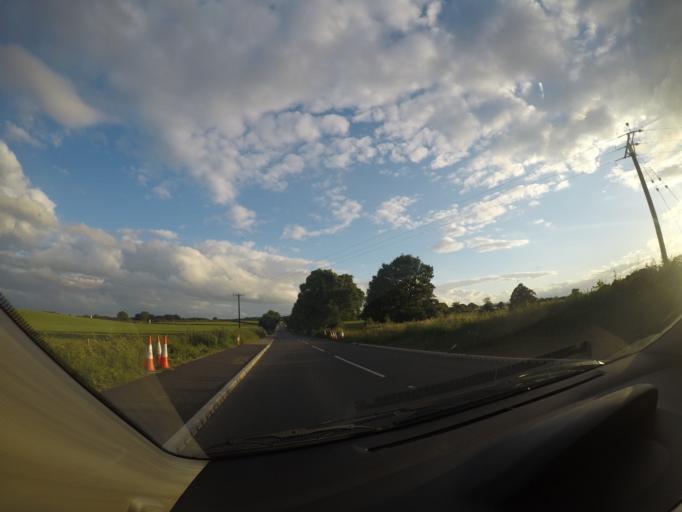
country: GB
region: England
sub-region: North Yorkshire
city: Catterick
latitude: 54.3850
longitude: -1.6561
